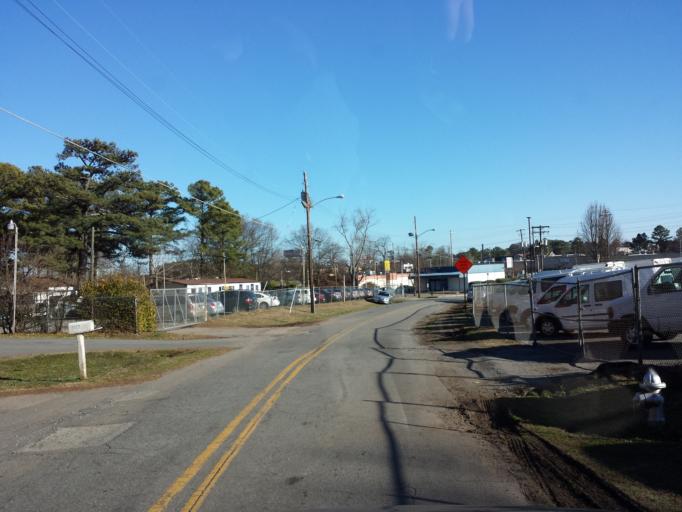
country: US
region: Georgia
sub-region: Cobb County
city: Marietta
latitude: 33.9522
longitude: -84.5194
